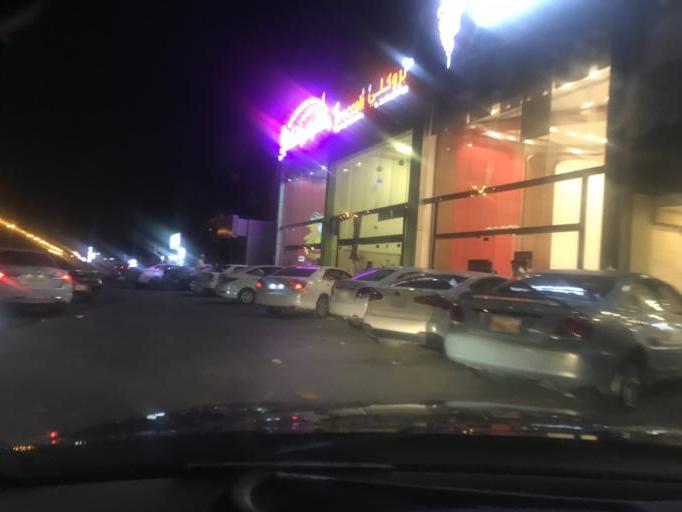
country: SA
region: Ar Riyad
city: Riyadh
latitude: 24.7432
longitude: 46.8087
